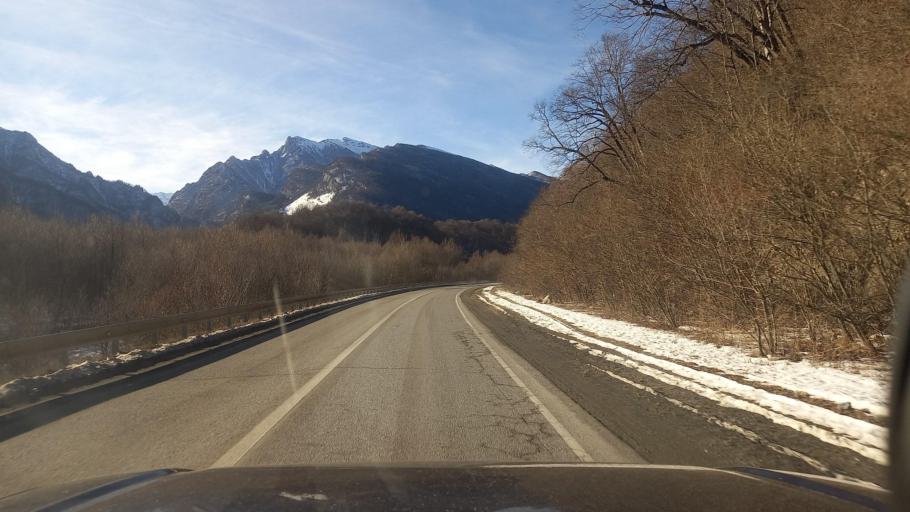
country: RU
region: North Ossetia
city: Gizel'
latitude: 42.9305
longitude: 44.5441
